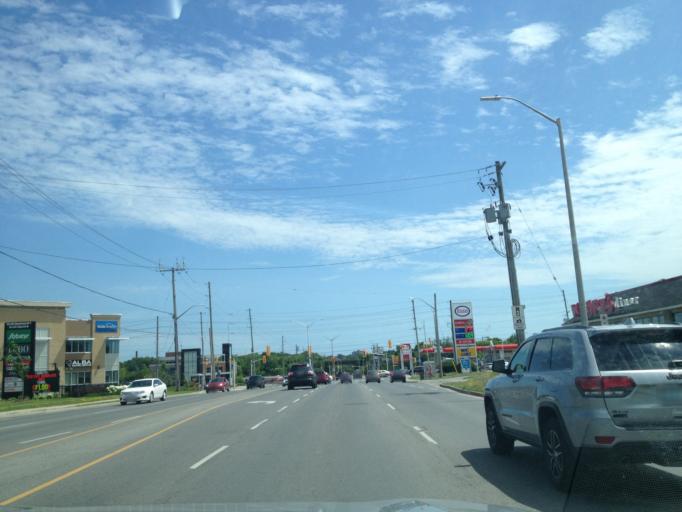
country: CA
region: Ontario
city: London
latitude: 42.9850
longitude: -81.2933
